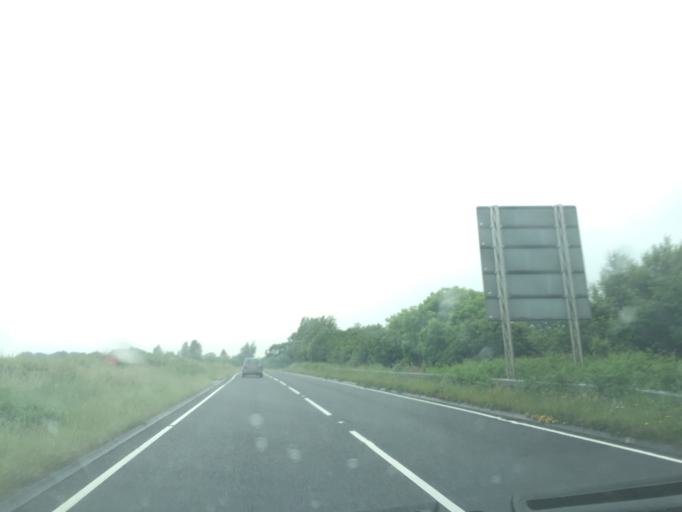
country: GB
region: England
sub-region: Dorset
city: Lytchett Matravers
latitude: 50.7331
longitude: -2.0693
